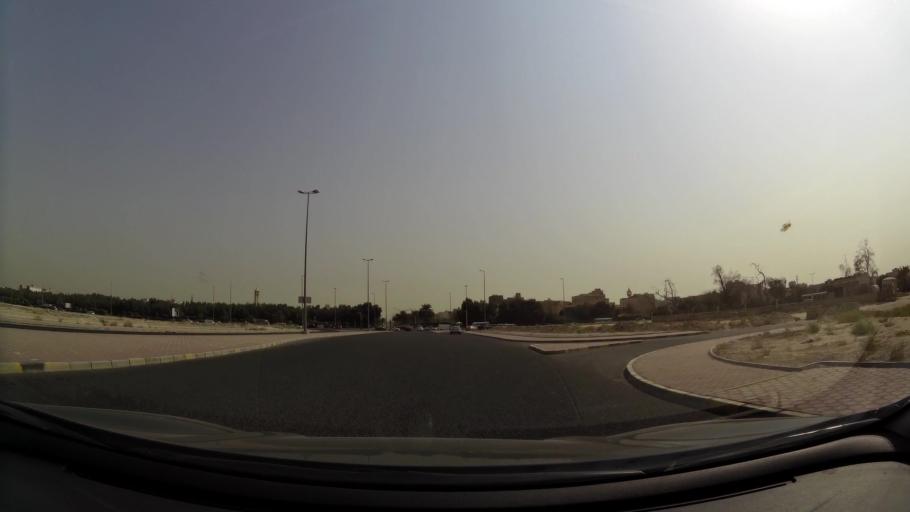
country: KW
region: Al Asimah
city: Ar Rabiyah
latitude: 29.2885
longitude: 47.9266
